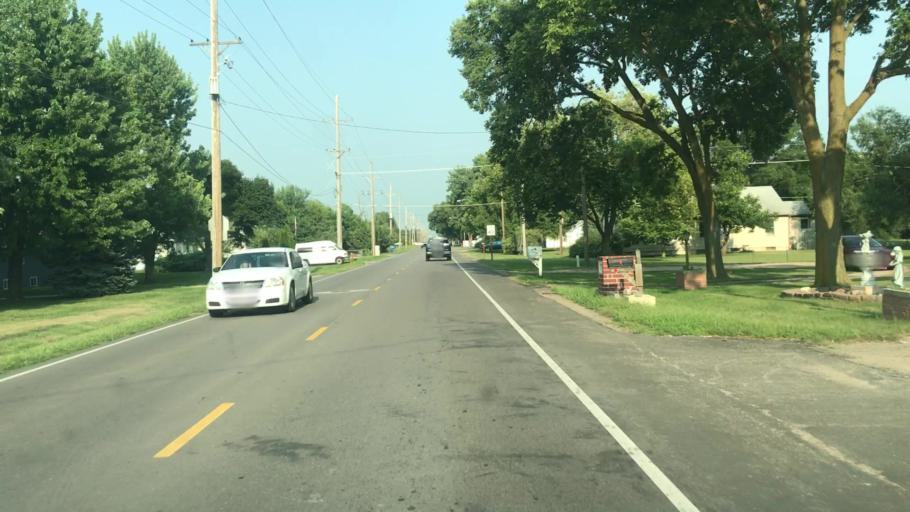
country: US
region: Nebraska
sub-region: Hall County
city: Grand Island
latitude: 40.9457
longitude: -98.3442
